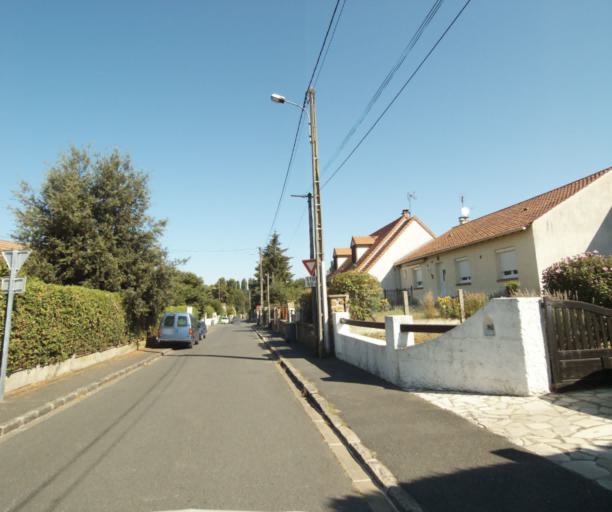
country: FR
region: Ile-de-France
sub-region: Departement de l'Essonne
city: Saint-Vrain
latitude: 48.5358
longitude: 2.3436
